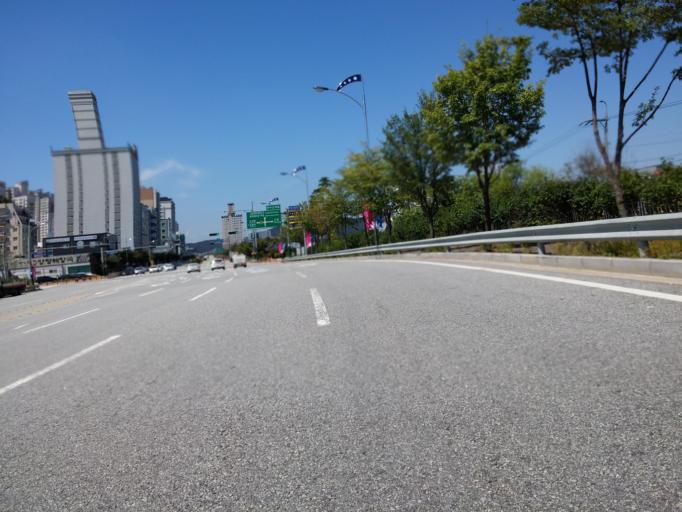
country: KR
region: Chungcheongbuk-do
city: Cheongju-si
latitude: 36.6297
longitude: 127.3349
